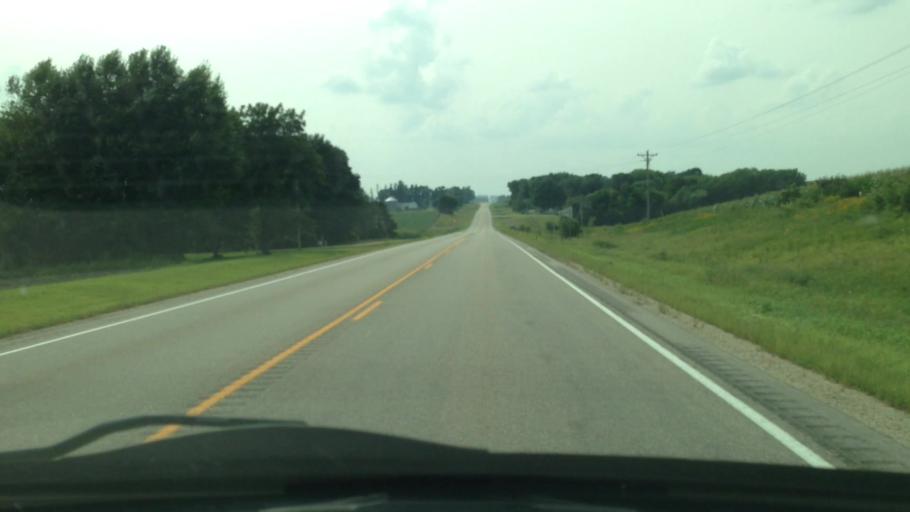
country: US
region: Minnesota
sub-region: Wabasha County
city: Elgin
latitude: 44.1654
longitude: -92.2449
